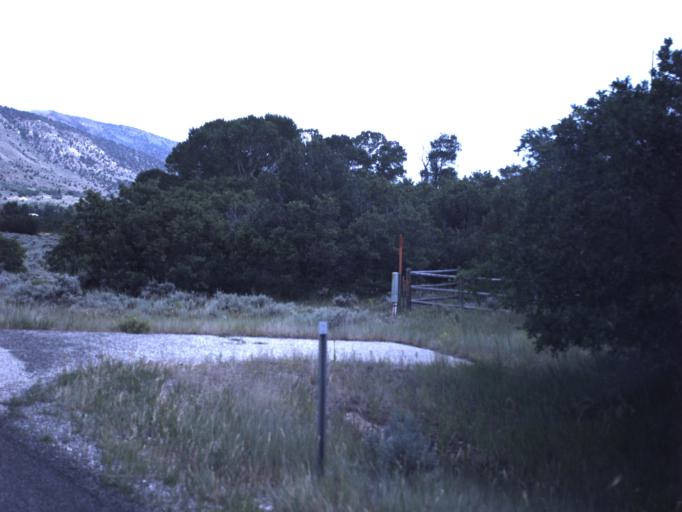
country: US
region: Utah
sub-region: Summit County
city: Francis
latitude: 40.4623
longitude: -110.8396
